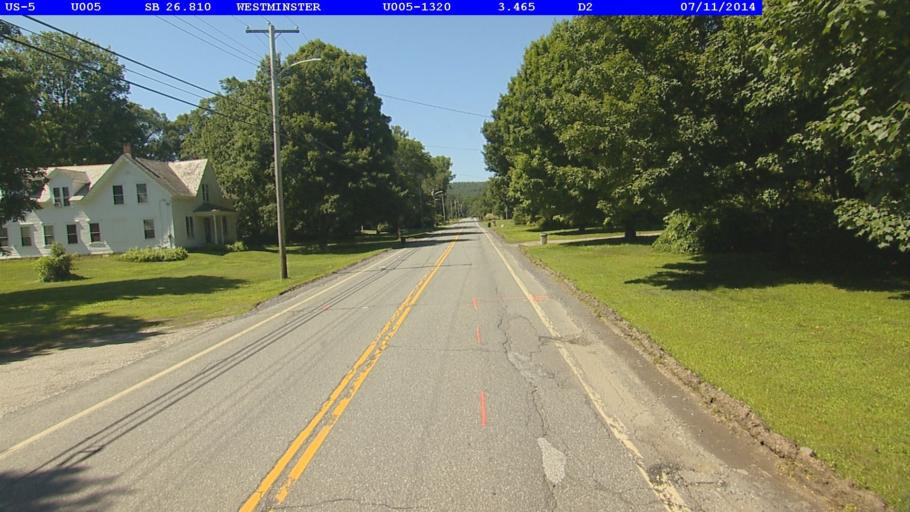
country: US
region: Vermont
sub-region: Windham County
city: Bellows Falls
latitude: 43.0666
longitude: -72.4600
